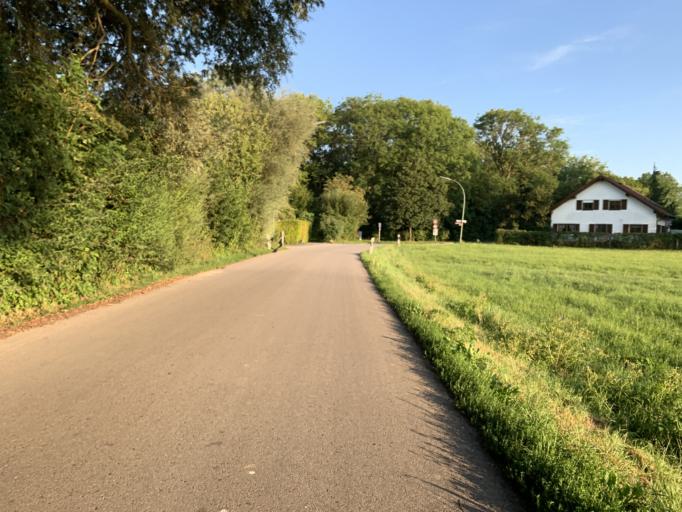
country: DE
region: Bavaria
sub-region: Upper Bavaria
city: Freising
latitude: 48.3902
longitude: 11.7271
